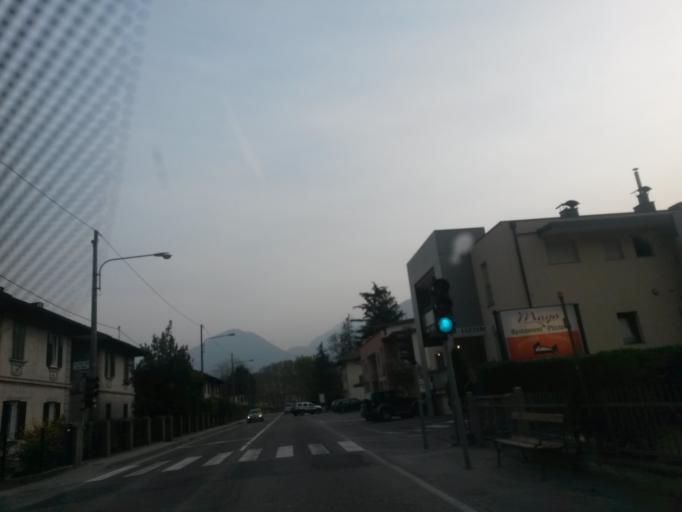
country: IT
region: Trentino-Alto Adige
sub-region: Bolzano
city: Sinigo
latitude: 46.6408
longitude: 11.1770
